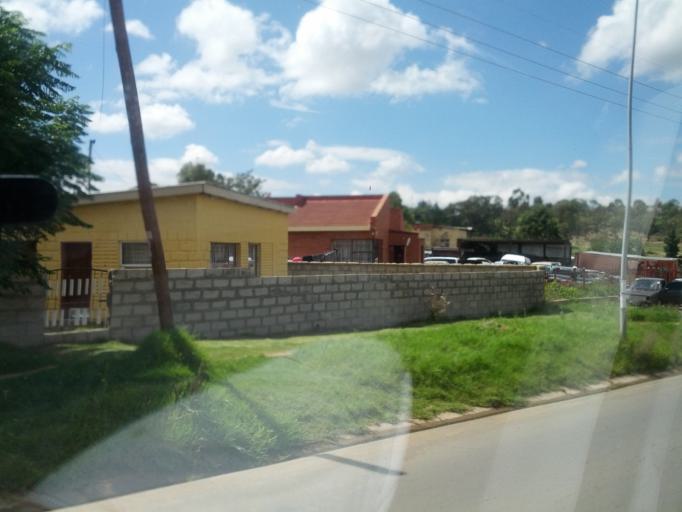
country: LS
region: Maseru
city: Maseru
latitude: -29.2956
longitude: 27.5175
